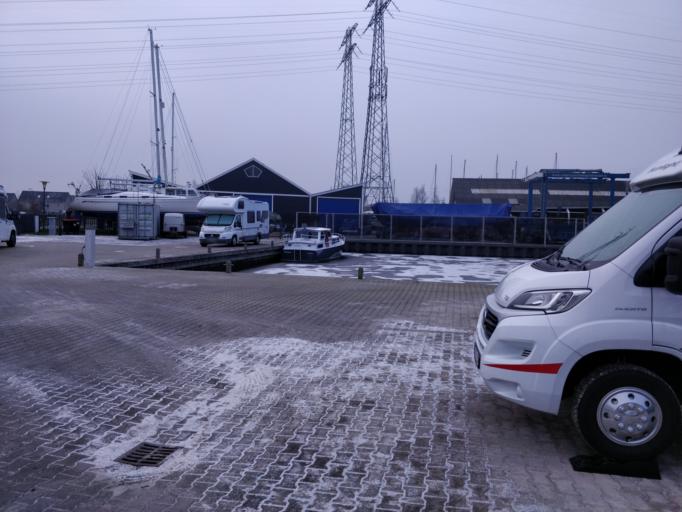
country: NL
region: Friesland
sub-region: Gemeente Leeuwarden
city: Camminghaburen
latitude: 53.1849
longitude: 5.8370
